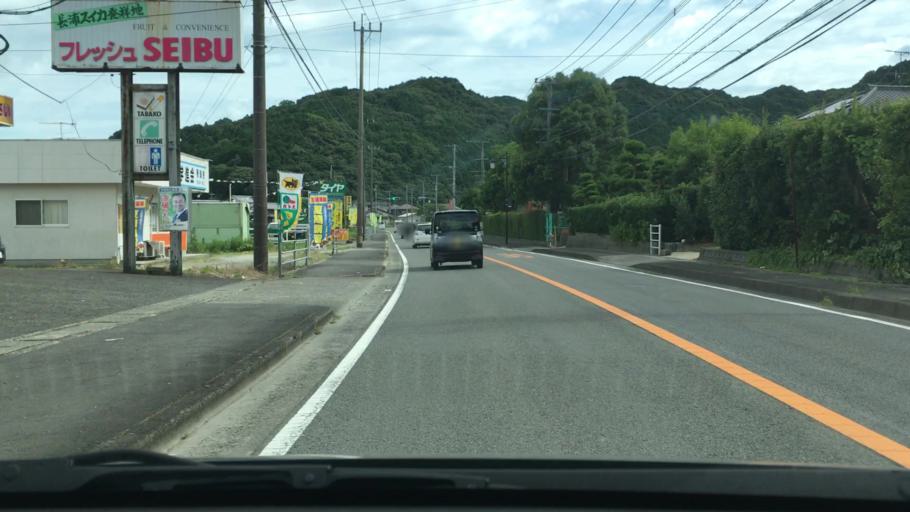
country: JP
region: Nagasaki
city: Togitsu
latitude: 32.8955
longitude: 129.7805
